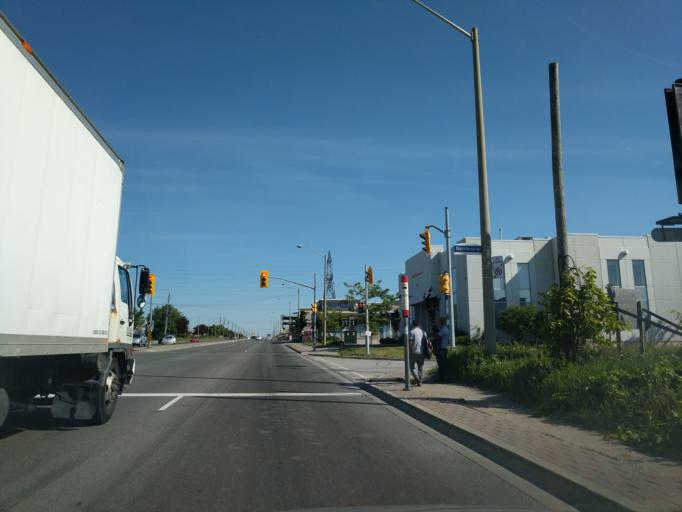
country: CA
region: Ontario
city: Scarborough
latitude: 43.8201
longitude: -79.2460
